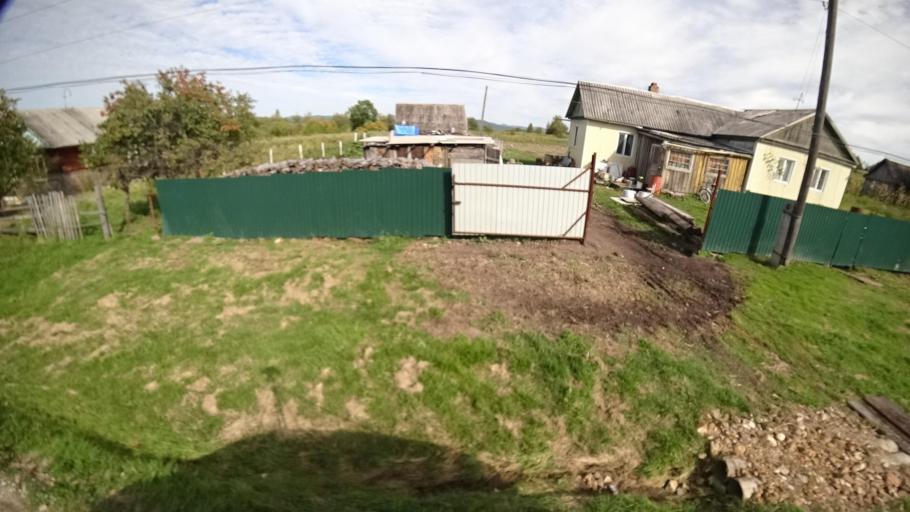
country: RU
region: Primorskiy
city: Dostoyevka
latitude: 44.3265
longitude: 133.4867
